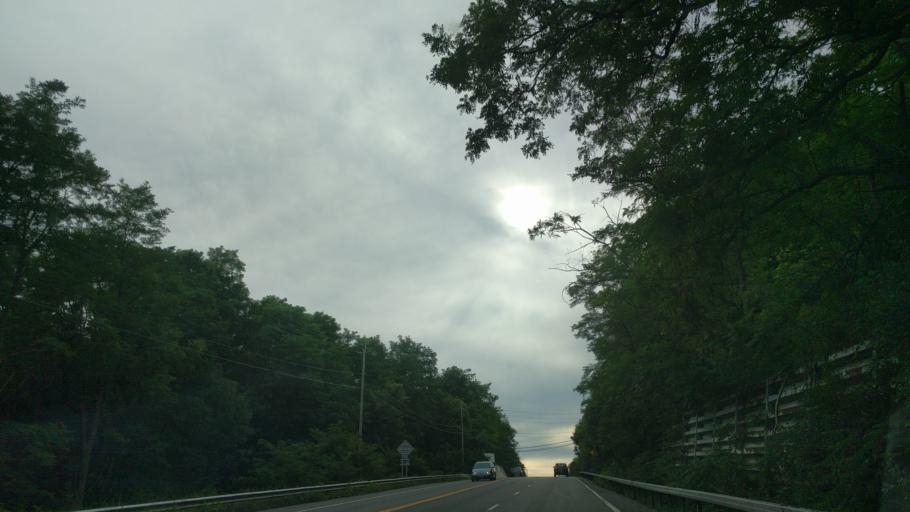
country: US
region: New York
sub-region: Onondaga County
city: Nedrow
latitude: 43.0056
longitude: -76.1657
